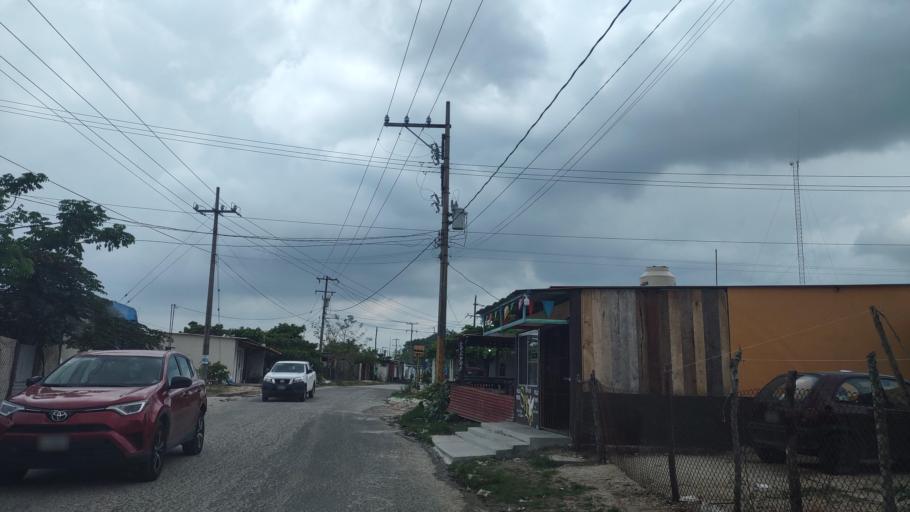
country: MX
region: Veracruz
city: Las Choapas
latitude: 17.9082
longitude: -94.1112
